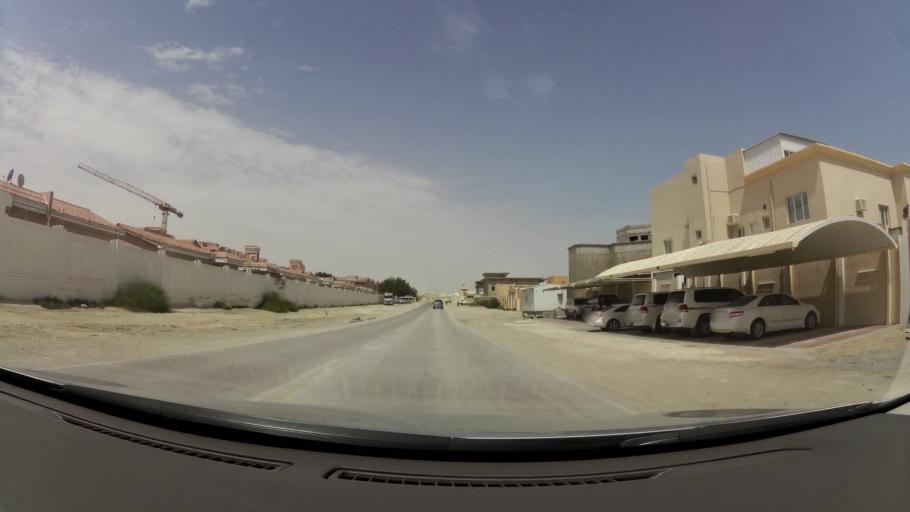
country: QA
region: Baladiyat ar Rayyan
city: Ar Rayyan
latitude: 25.3494
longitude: 51.4703
